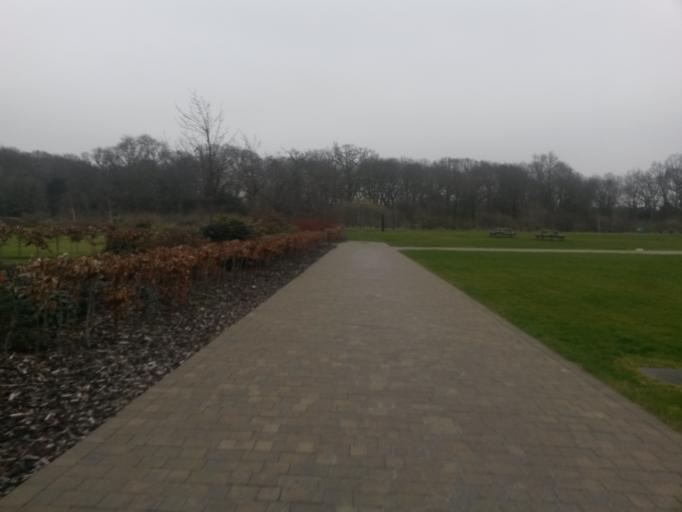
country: GB
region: England
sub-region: Hampshire
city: Totton
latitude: 50.9388
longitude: -1.4701
